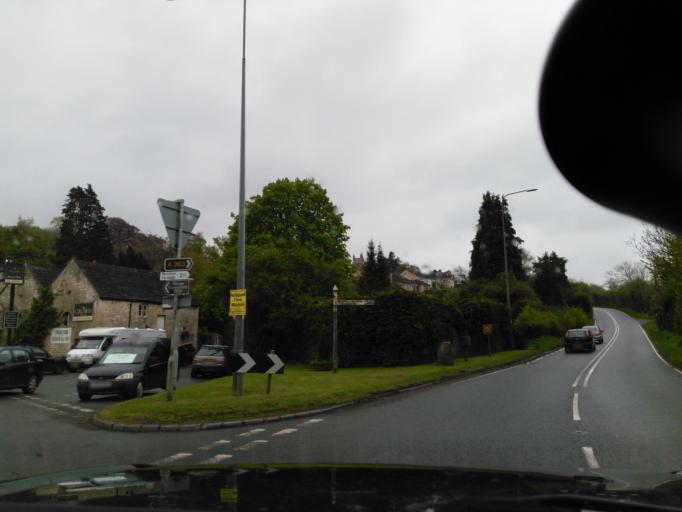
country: GB
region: England
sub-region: Wiltshire
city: Colerne
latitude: 51.4012
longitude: -2.3078
